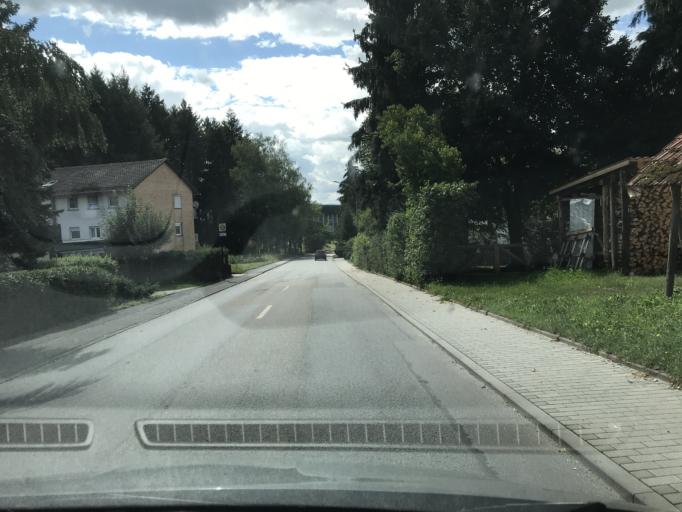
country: DE
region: Hesse
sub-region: Regierungsbezirk Darmstadt
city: Lindenfels
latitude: 49.6659
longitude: 8.7449
